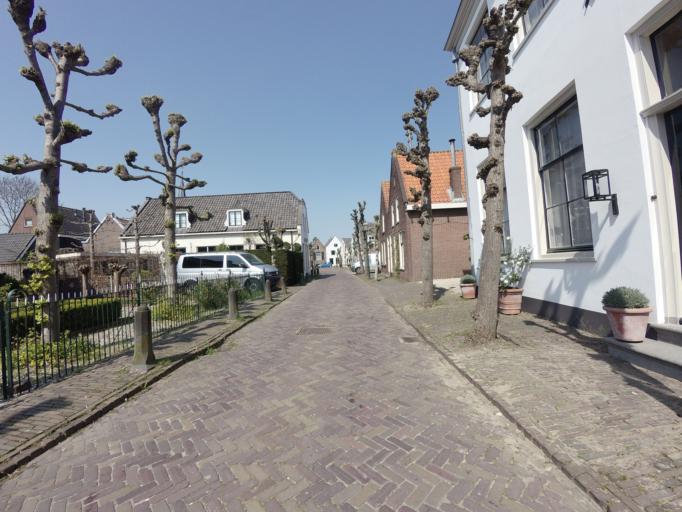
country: NL
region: Utrecht
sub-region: Stichtse Vecht
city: Vreeland
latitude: 52.2459
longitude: 4.9905
